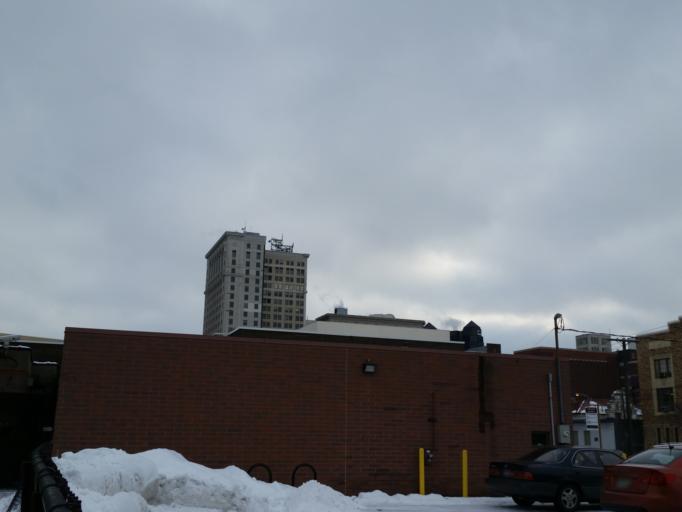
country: US
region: Ohio
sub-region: Cuyahoga County
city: Cleveland
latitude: 41.5043
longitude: -81.6800
